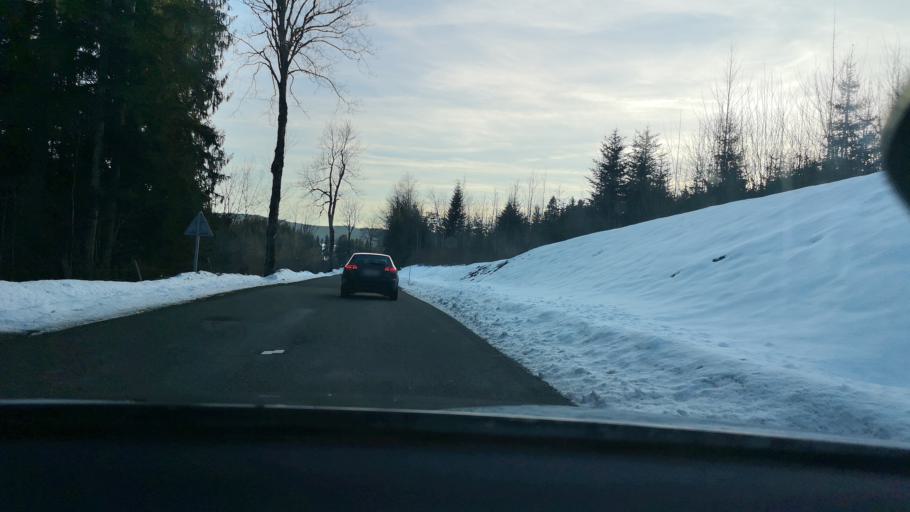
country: FR
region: Franche-Comte
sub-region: Departement du Doubs
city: La Cluse-et-Mijoux
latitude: 46.9156
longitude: 6.3859
